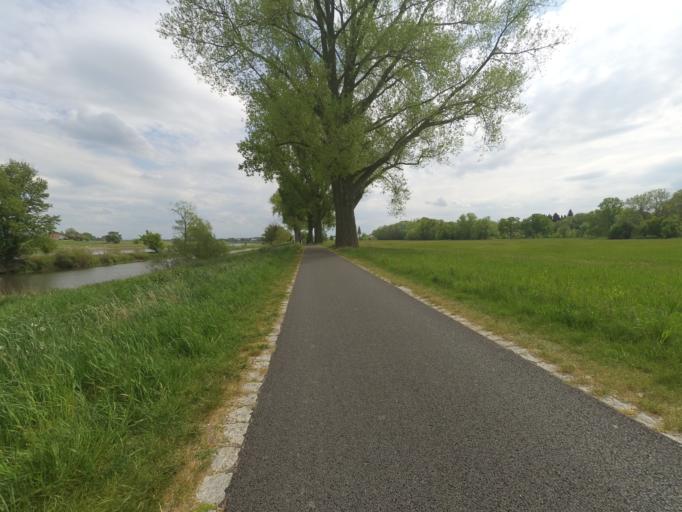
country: DE
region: Saxony
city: Strehla
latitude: 51.3575
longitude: 13.2303
